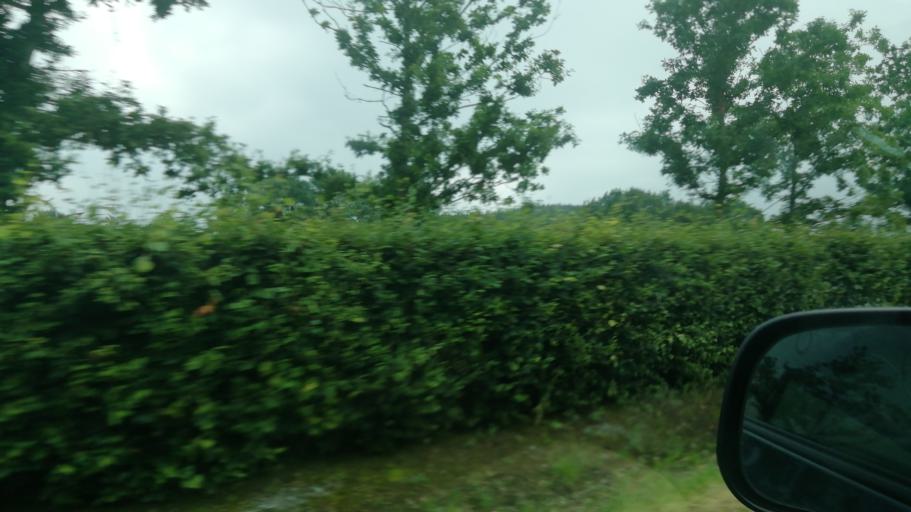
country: IE
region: Munster
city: Fethard
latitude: 52.4878
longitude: -7.6923
